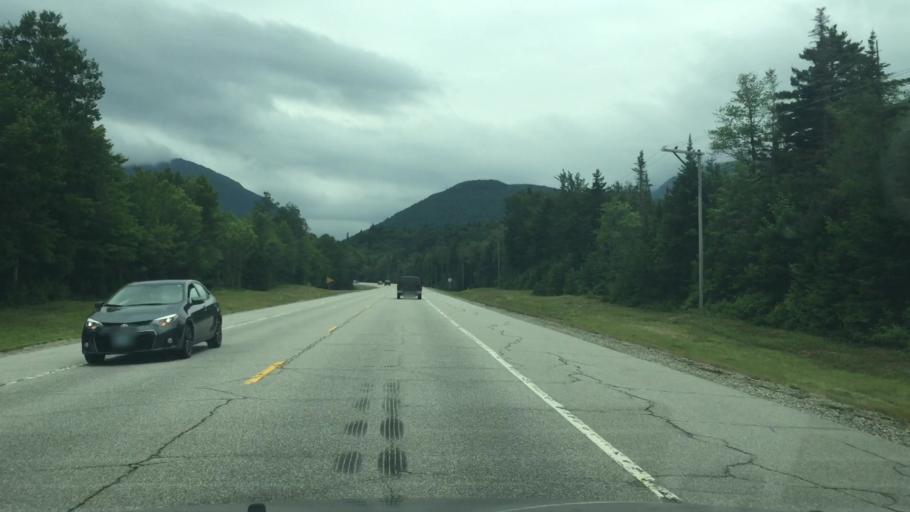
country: US
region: New Hampshire
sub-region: Coos County
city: Jefferson
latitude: 44.2305
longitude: -71.4202
